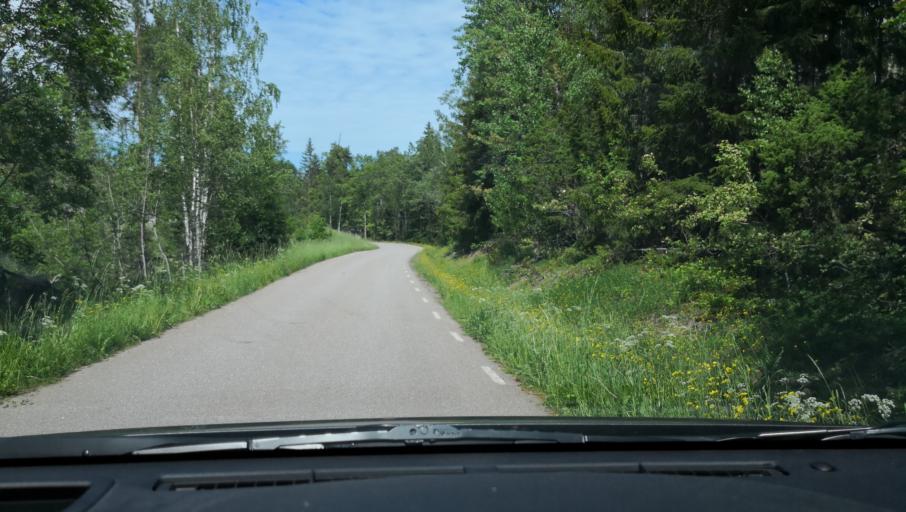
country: SE
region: Uppsala
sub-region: Uppsala Kommun
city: Alsike
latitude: 59.7022
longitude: 17.6505
